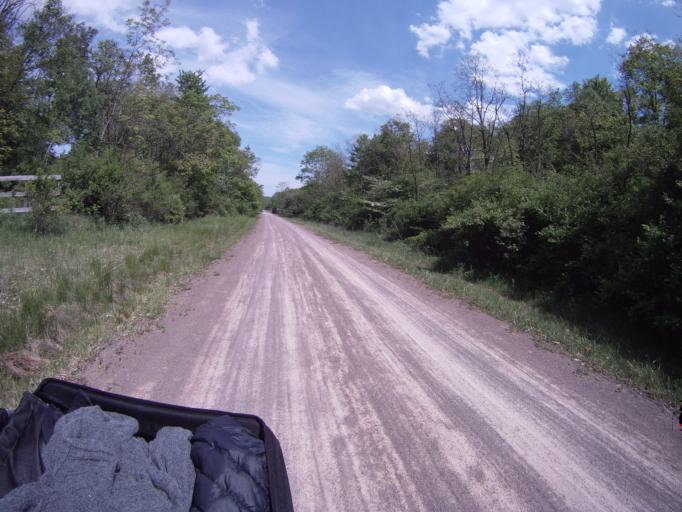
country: US
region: Pennsylvania
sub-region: Somerset County
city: Meyersdale
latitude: 39.7967
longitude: -78.9804
